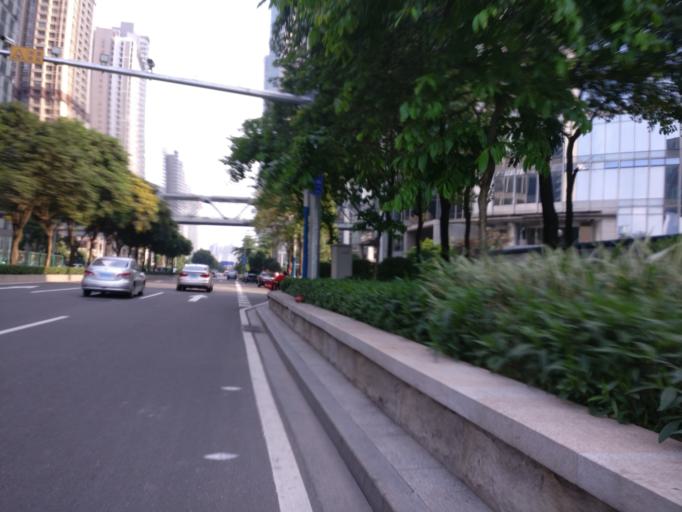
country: CN
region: Guangdong
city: Wushan
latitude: 23.1251
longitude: 113.3225
